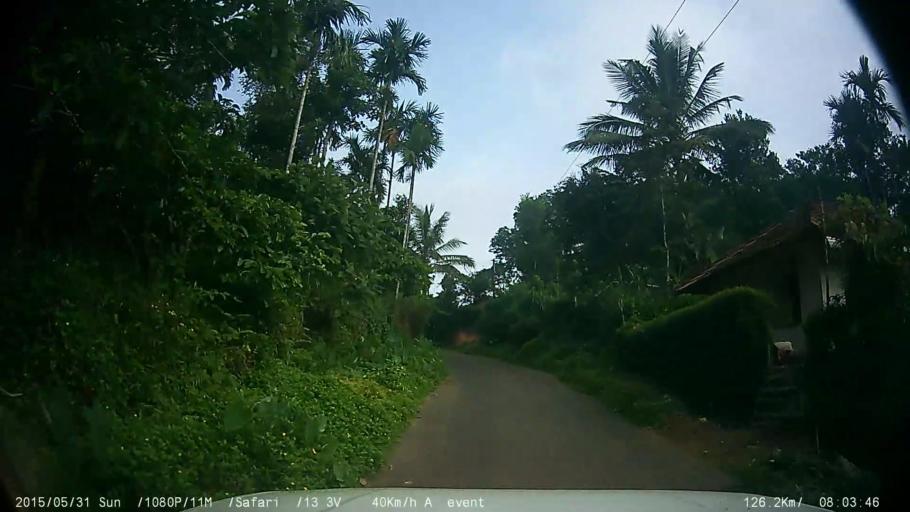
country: IN
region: Kerala
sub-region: Wayanad
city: Kalpetta
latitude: 11.6369
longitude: 76.0418
